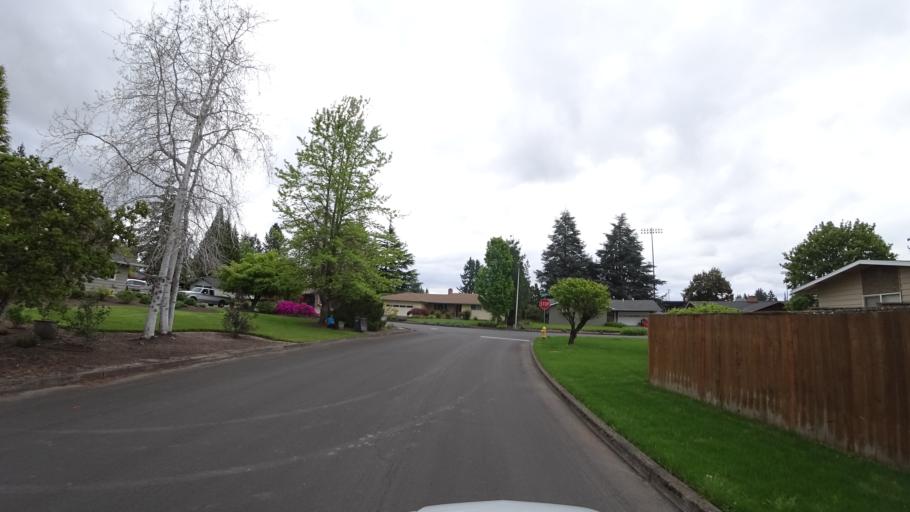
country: US
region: Oregon
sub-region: Washington County
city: Hillsboro
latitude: 45.5301
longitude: -122.9744
